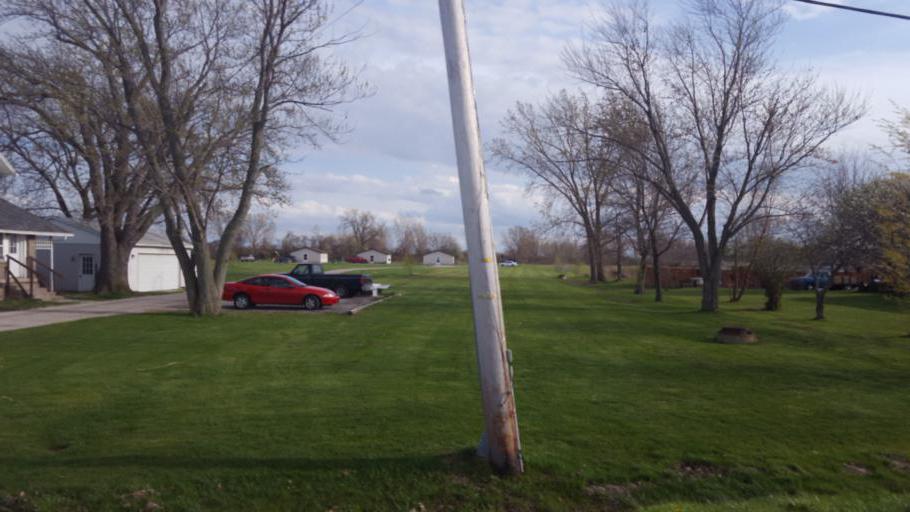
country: US
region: Ohio
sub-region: Ottawa County
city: Port Clinton
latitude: 41.5040
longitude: -82.8247
